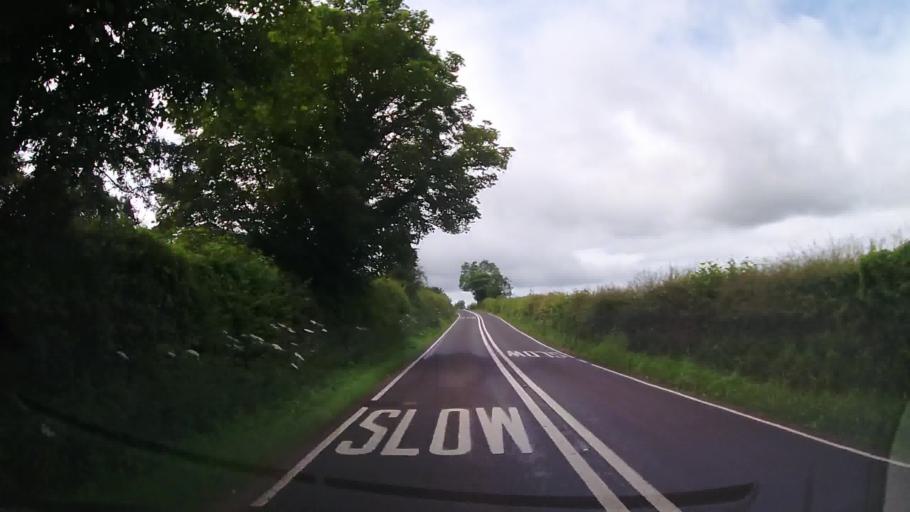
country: GB
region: England
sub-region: Shropshire
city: Gobowen
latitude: 52.9254
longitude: -2.9887
